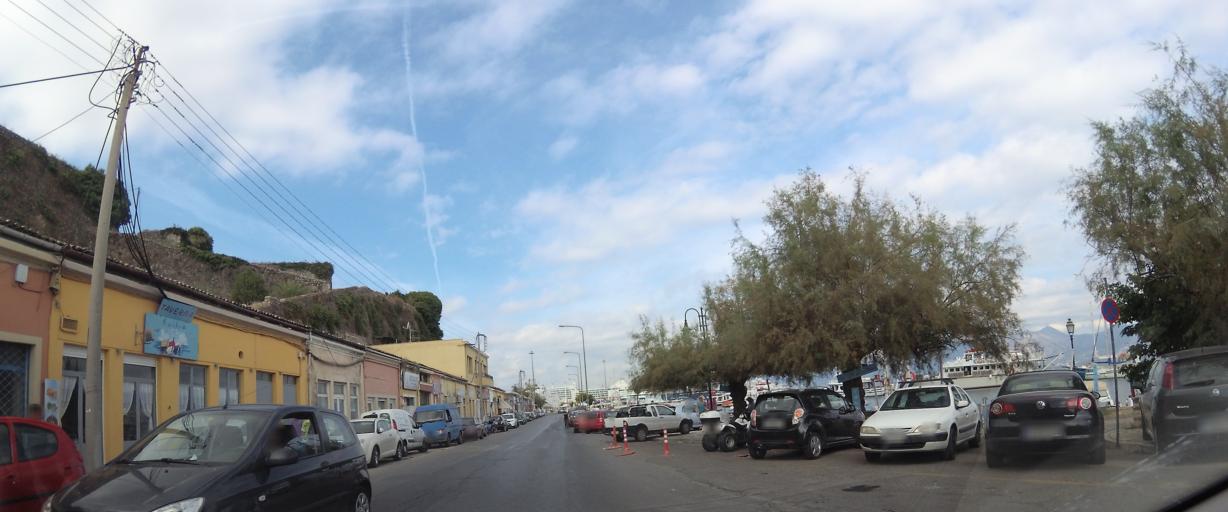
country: GR
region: Ionian Islands
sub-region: Nomos Kerkyras
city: Kerkyra
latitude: 39.6266
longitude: 19.9172
